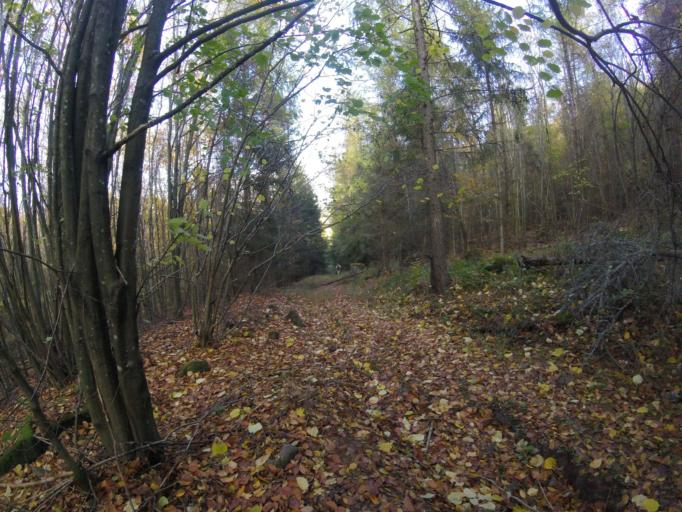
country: HU
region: Borsod-Abauj-Zemplen
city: Tolcsva
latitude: 48.3733
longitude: 21.3795
